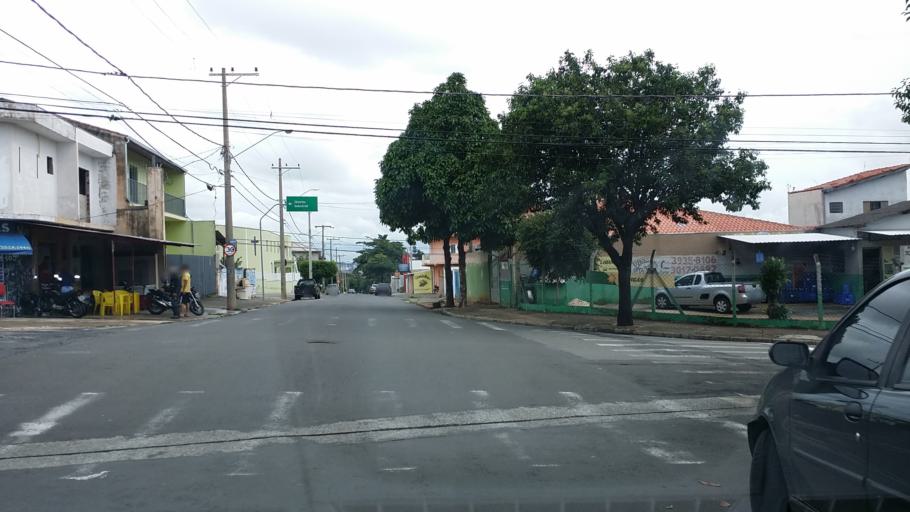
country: BR
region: Sao Paulo
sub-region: Indaiatuba
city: Indaiatuba
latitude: -23.1225
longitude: -47.2282
